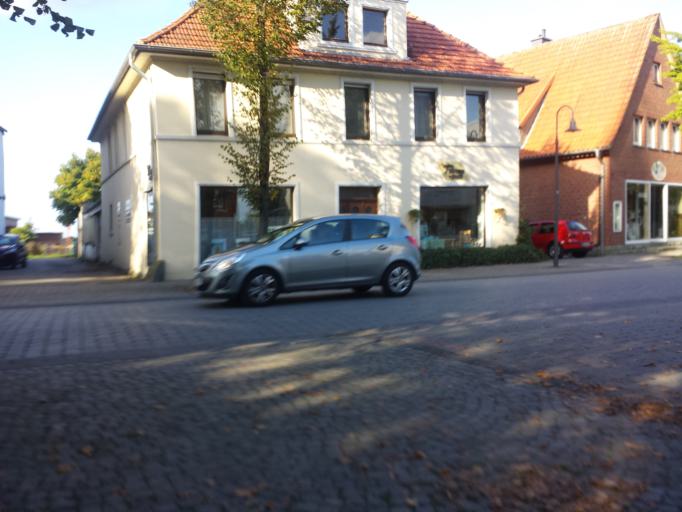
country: DE
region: North Rhine-Westphalia
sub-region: Regierungsbezirk Detmold
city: Langenberg
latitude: 51.7756
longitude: 8.3166
